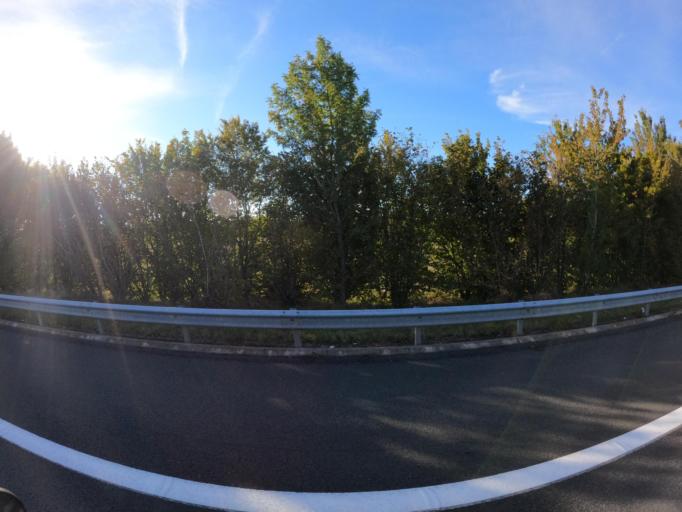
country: FR
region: Pays de la Loire
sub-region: Departement de Maine-et-Loire
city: Saint-Lambert-du-Lattay
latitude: 47.2940
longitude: -0.6123
